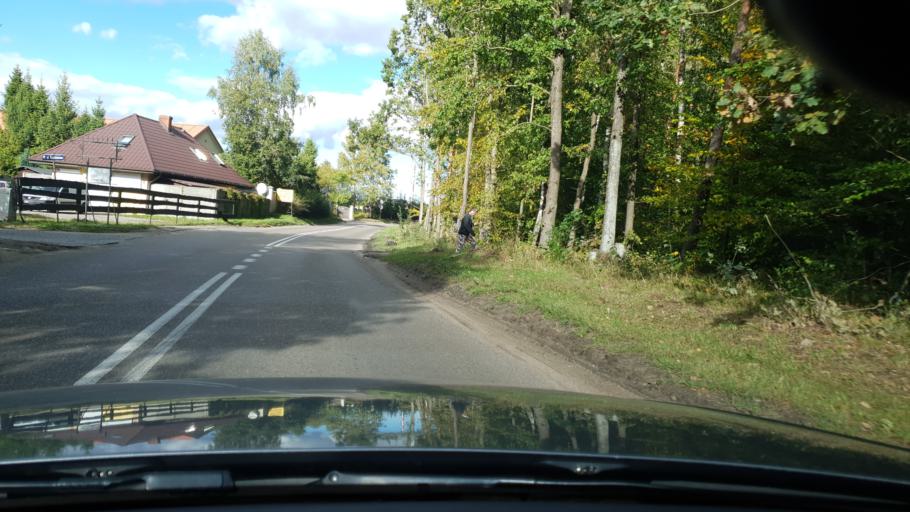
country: PL
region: Pomeranian Voivodeship
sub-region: Powiat wejherowski
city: Bojano
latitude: 54.5071
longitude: 18.3806
